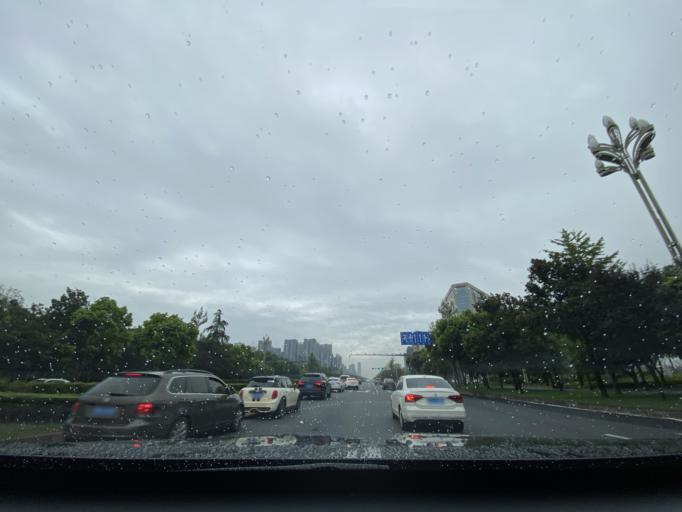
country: CN
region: Sichuan
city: Chengdu
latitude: 30.5234
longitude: 104.0673
